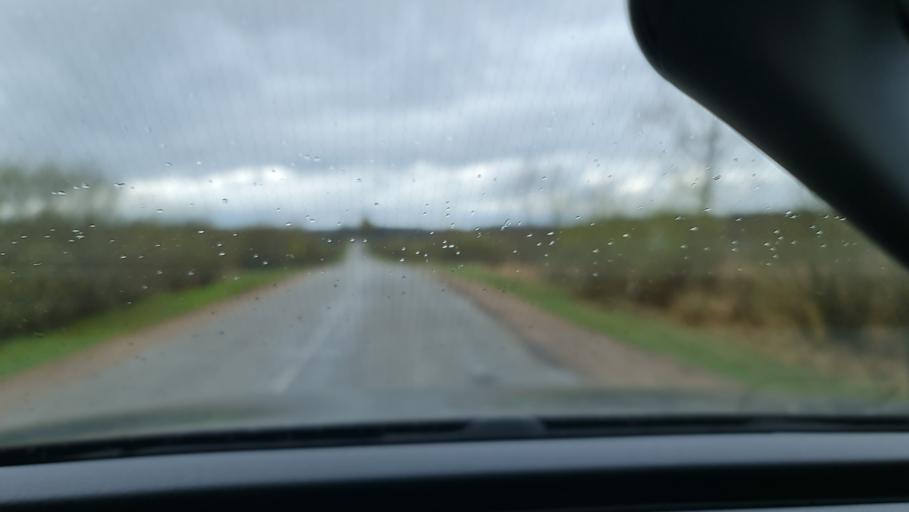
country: RU
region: Novgorod
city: Marevo
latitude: 57.2446
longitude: 32.0549
